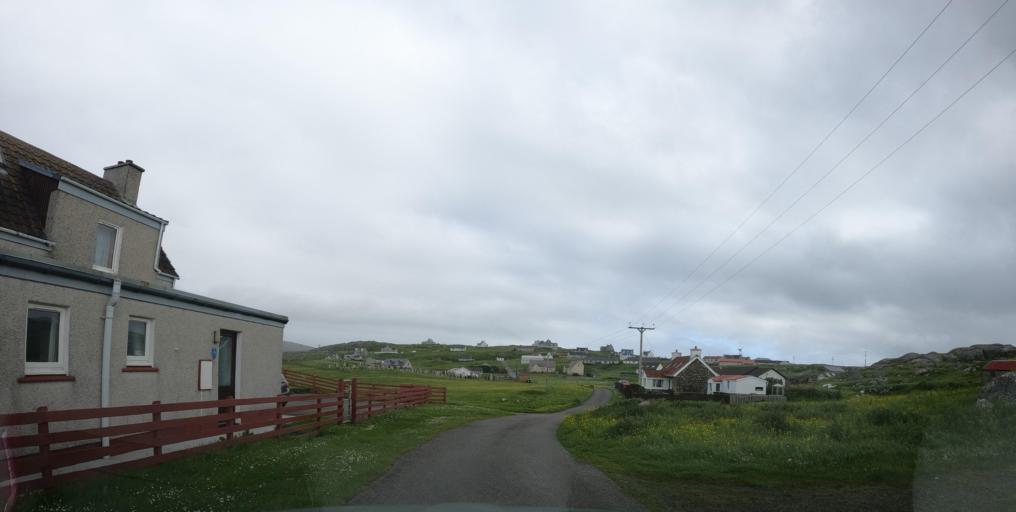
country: GB
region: Scotland
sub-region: Eilean Siar
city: Isle of South Uist
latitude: 57.0824
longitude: -7.3099
